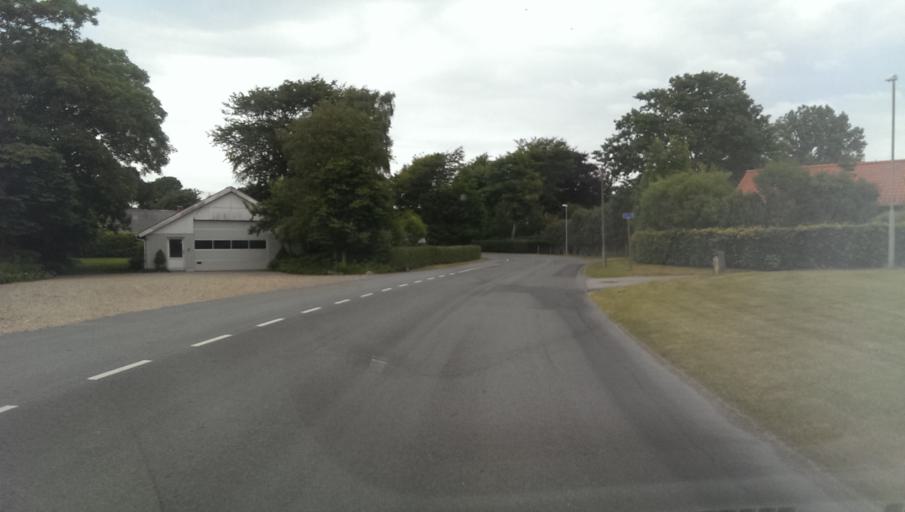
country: DK
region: South Denmark
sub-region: Esbjerg Kommune
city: Bramming
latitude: 55.4281
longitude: 8.6474
